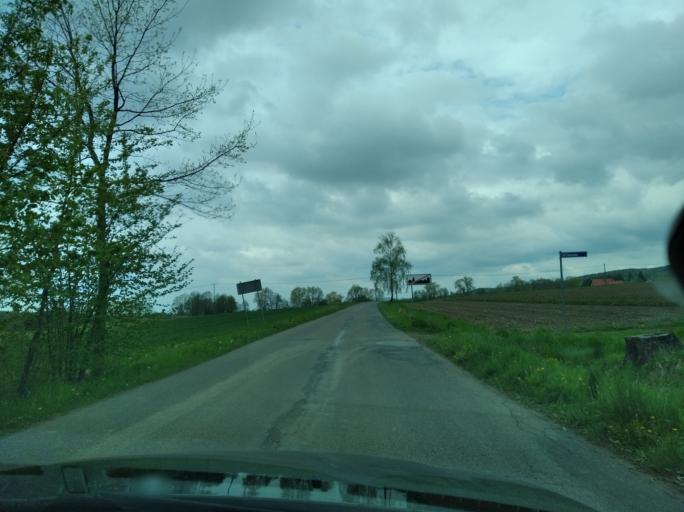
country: PL
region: Subcarpathian Voivodeship
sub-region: Powiat sanocki
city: Dlugie
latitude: 49.6068
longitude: 22.0492
